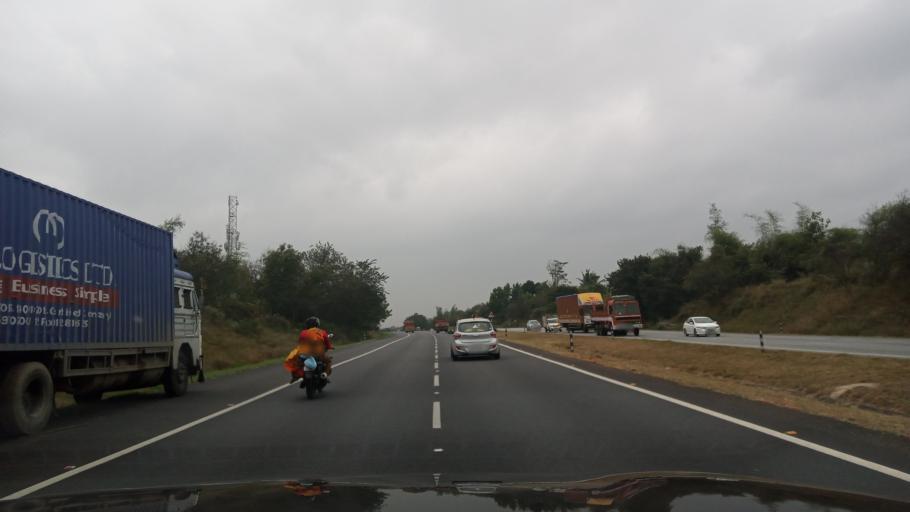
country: IN
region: Karnataka
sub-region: Bangalore Rural
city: Nelamangala
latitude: 13.0086
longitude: 77.4750
